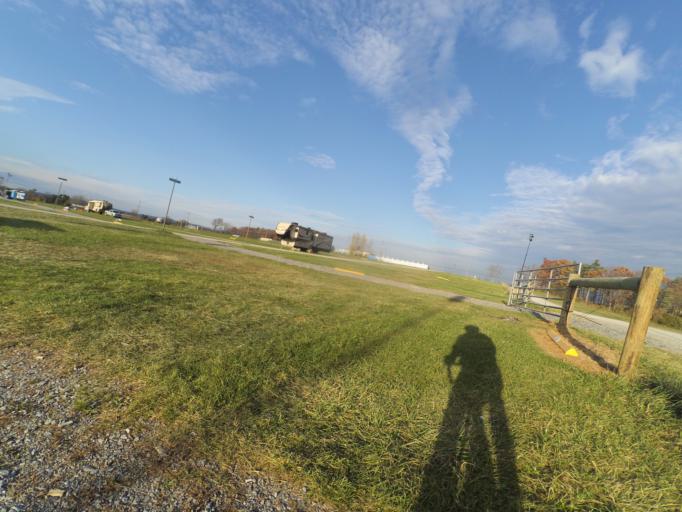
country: US
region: Pennsylvania
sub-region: Centre County
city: Houserville
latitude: 40.8189
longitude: -77.8540
